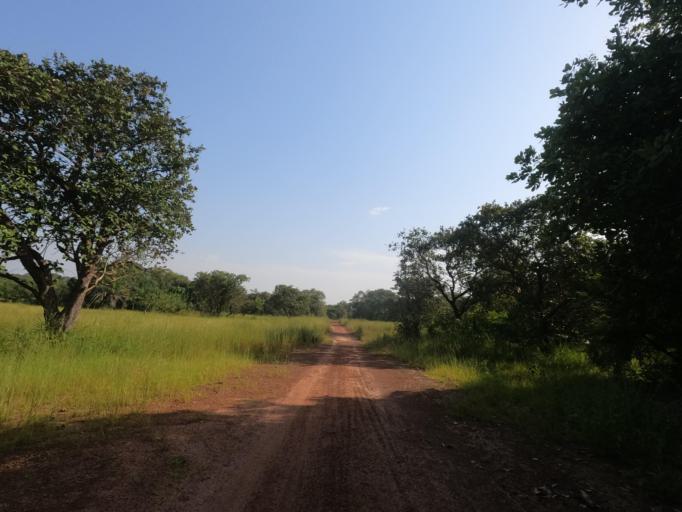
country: SN
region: Sedhiou
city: Sedhiou
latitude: 12.4347
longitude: -15.7378
